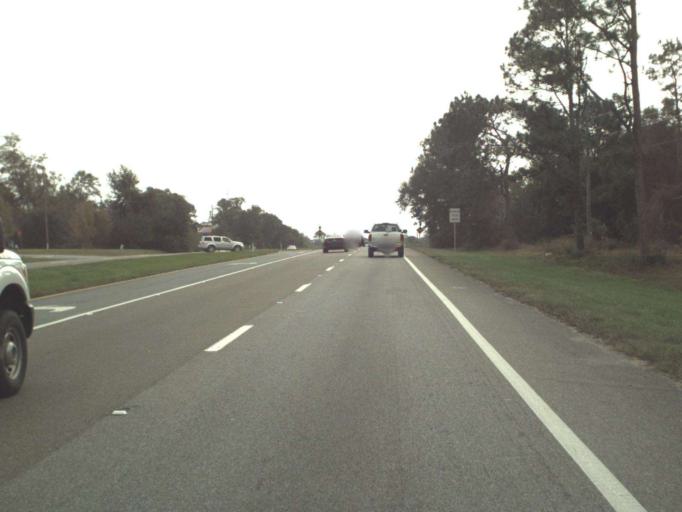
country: US
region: Florida
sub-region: Escambia County
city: Gonzalez
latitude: 30.5838
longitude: -87.3012
